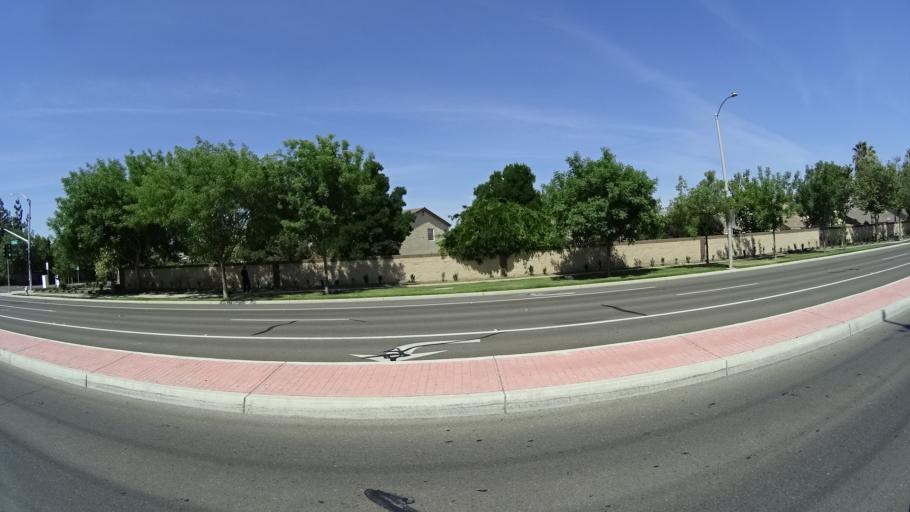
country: US
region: California
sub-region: Kings County
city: Hanford
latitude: 36.3332
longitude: -119.6729
